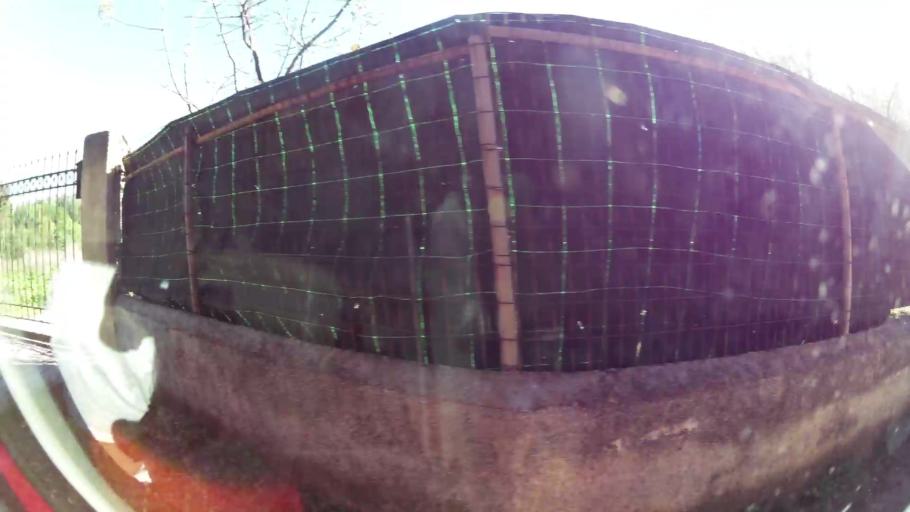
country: GR
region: Attica
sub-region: Nomarchia Anatolikis Attikis
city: Pallini
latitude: 37.9947
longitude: 23.8675
